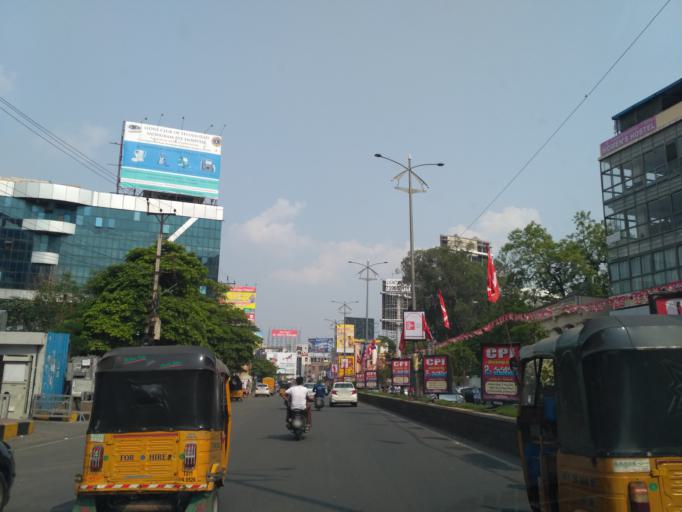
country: IN
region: Telangana
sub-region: Hyderabad
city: Hyderabad
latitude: 17.4013
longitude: 78.4859
